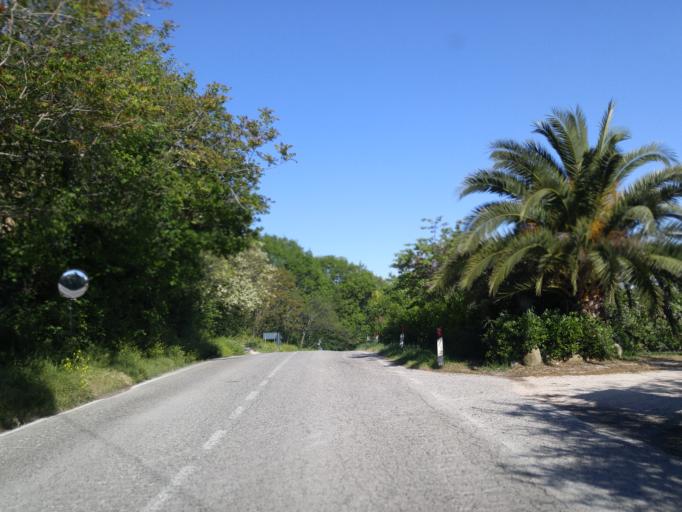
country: IT
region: The Marches
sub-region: Provincia di Pesaro e Urbino
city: Monteciccardo
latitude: 43.8328
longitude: 12.8235
